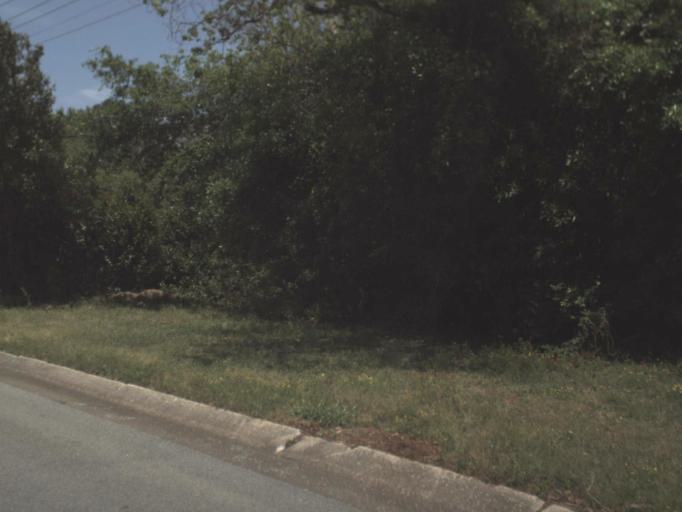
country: US
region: Florida
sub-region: Escambia County
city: Goulding
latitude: 30.4585
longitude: -87.1986
